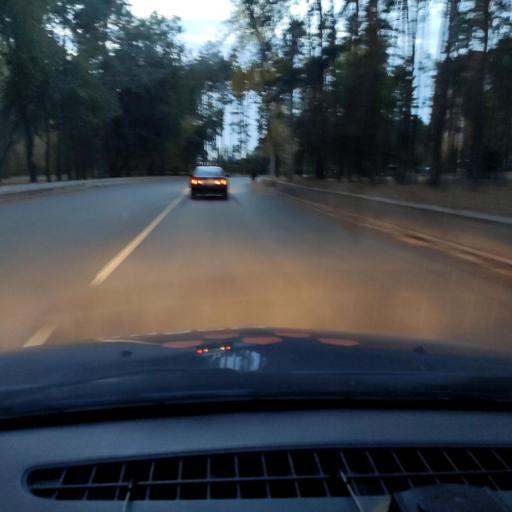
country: RU
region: Voronezj
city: Pridonskoy
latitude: 51.6846
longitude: 39.0817
